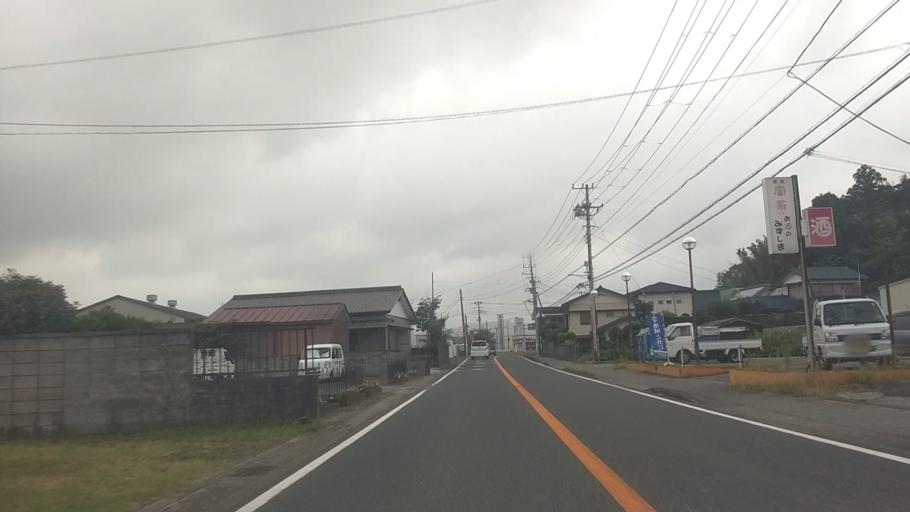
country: JP
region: Chiba
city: Kawaguchi
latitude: 35.1102
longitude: 140.0827
